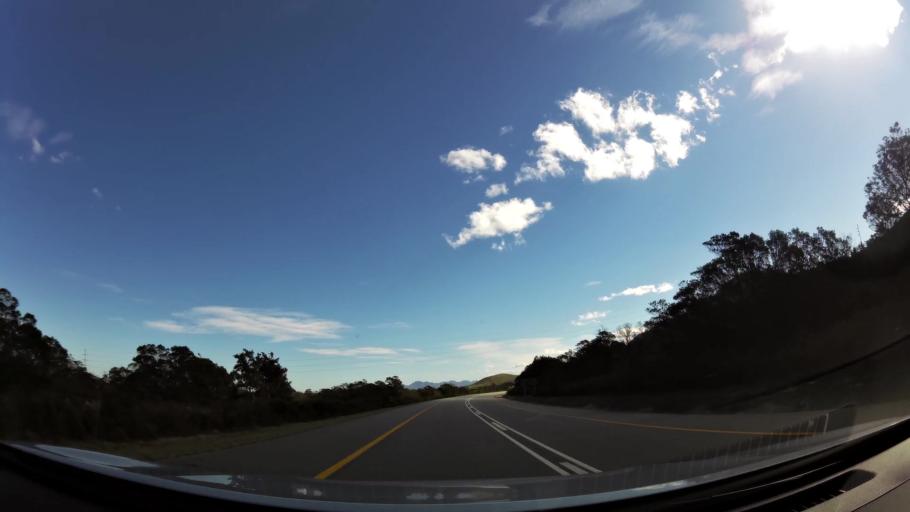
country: ZA
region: Eastern Cape
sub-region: Cacadu District Municipality
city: Kruisfontein
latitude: -33.9957
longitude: 24.7109
